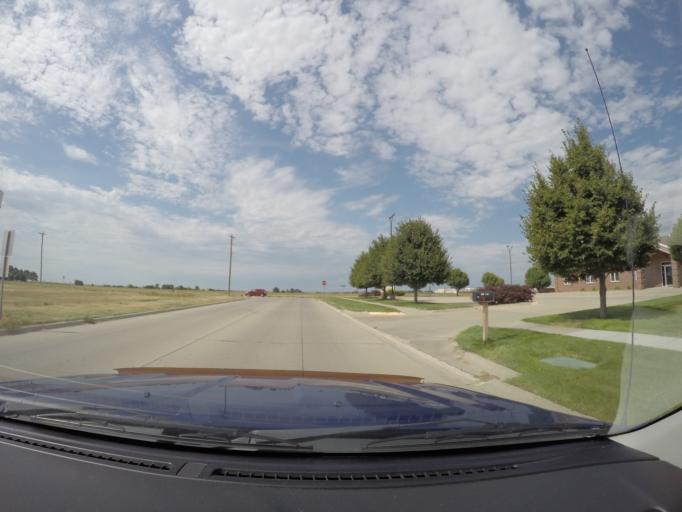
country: US
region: Nebraska
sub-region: Buffalo County
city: Kearney
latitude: 40.7207
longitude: -99.0911
